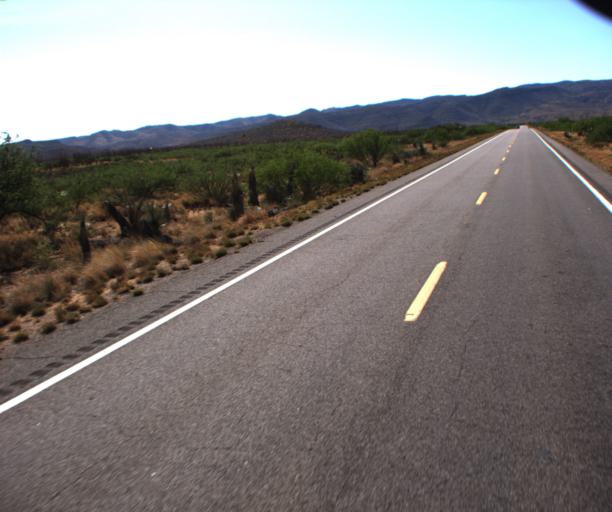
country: US
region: Arizona
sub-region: Cochise County
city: Bisbee
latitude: 31.5580
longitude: -110.0191
